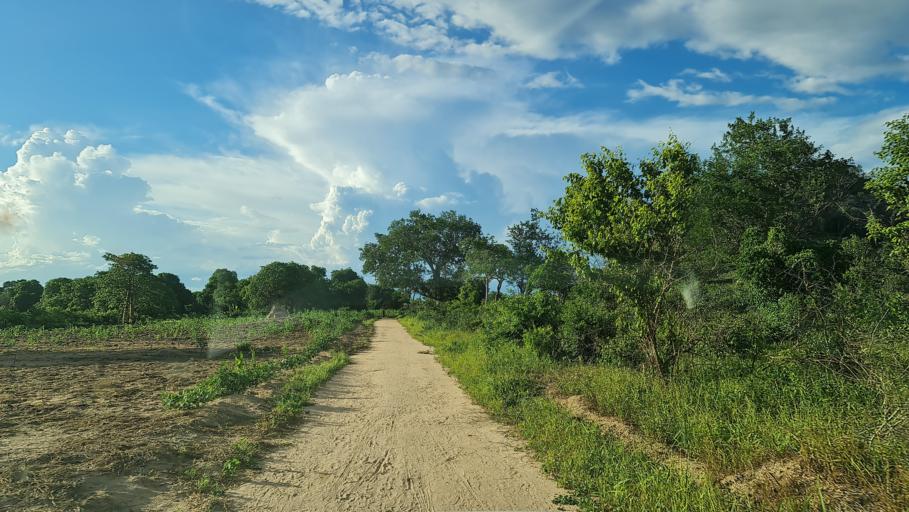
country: MZ
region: Nampula
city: Ilha de Mocambique
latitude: -14.9456
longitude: 40.1678
